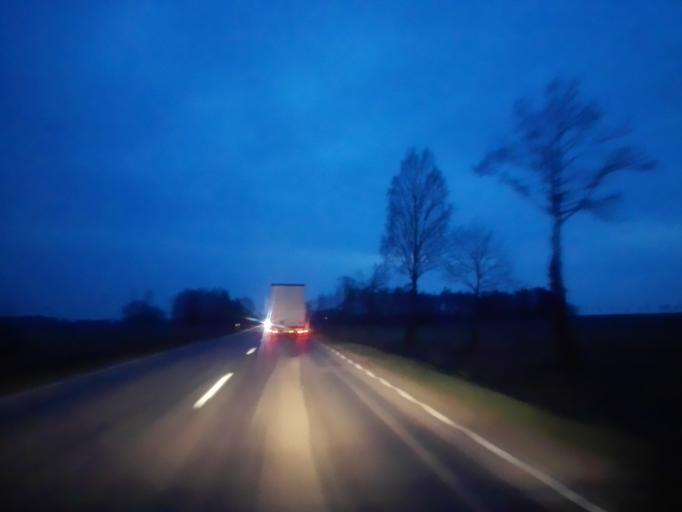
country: PL
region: Podlasie
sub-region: Powiat lomzynski
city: Sniadowo
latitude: 53.0561
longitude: 21.9981
